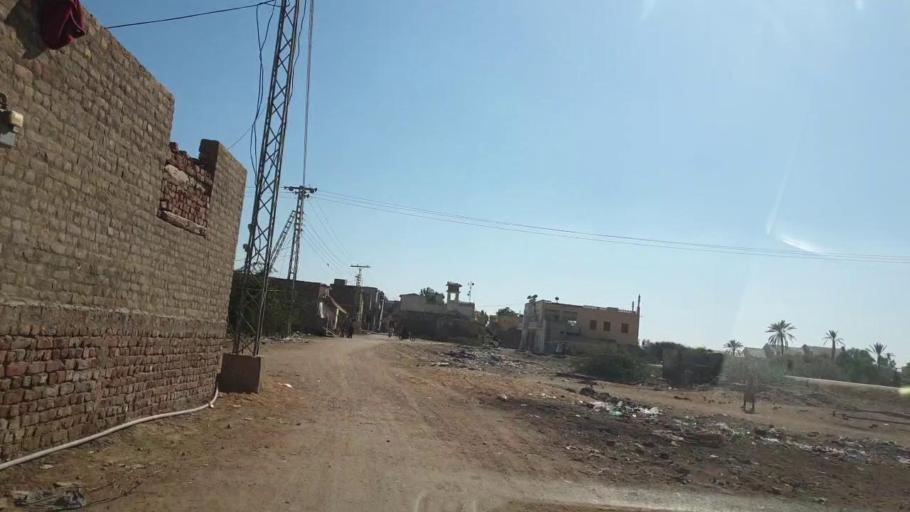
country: PK
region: Sindh
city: Berani
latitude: 25.8140
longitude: 68.9424
